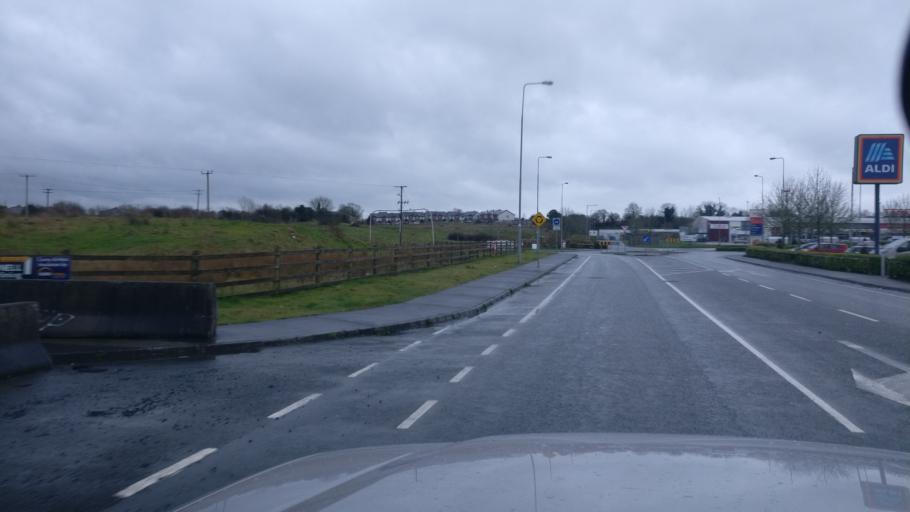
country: IE
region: Connaught
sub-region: County Galway
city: Ballinasloe
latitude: 53.3248
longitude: -8.2225
